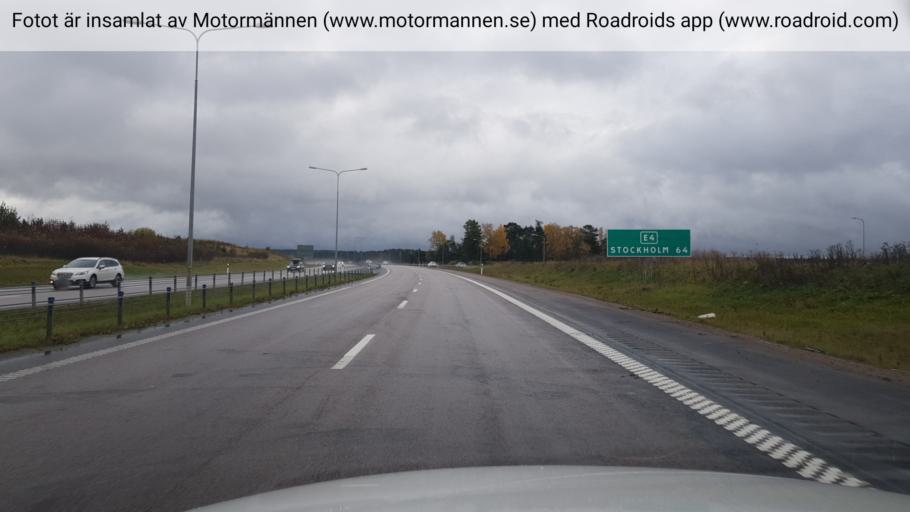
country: SE
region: Uppsala
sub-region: Uppsala Kommun
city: Saevja
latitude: 59.8365
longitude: 17.7311
